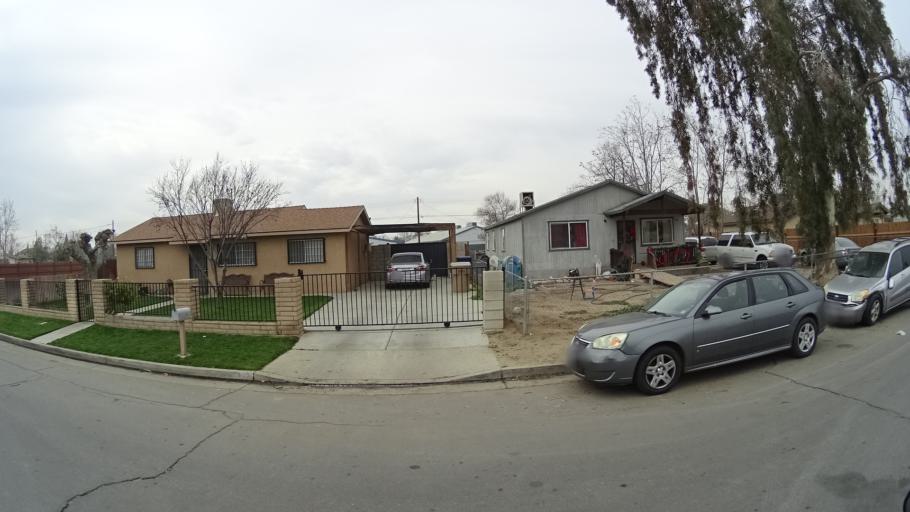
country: US
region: California
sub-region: Kern County
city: Bakersfield
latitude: 35.3569
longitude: -118.9956
